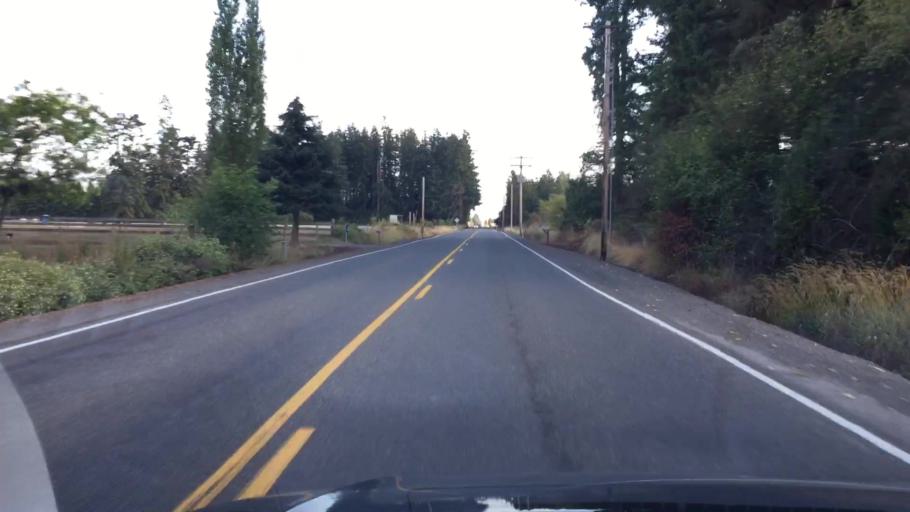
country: US
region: Washington
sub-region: Lewis County
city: Napavine
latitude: 46.5317
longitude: -122.7405
